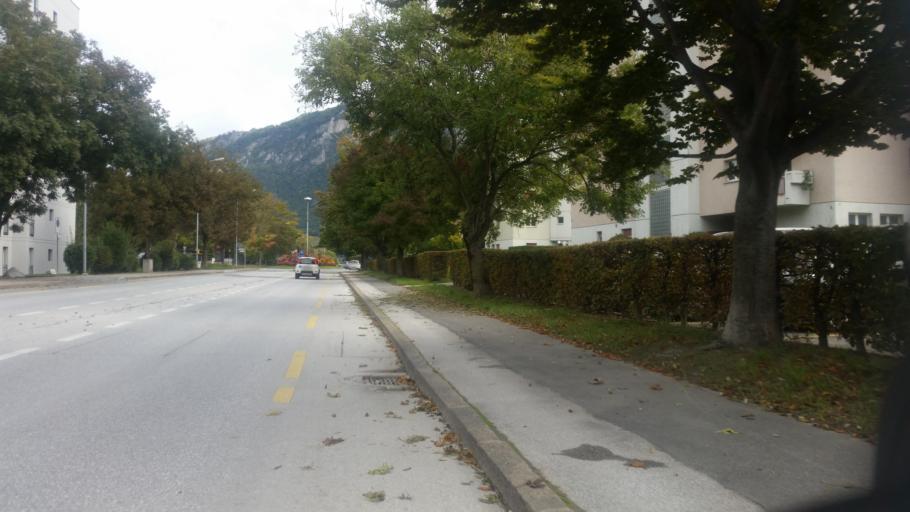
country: CH
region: Valais
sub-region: Sion District
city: Sitten
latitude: 46.2308
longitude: 7.3804
